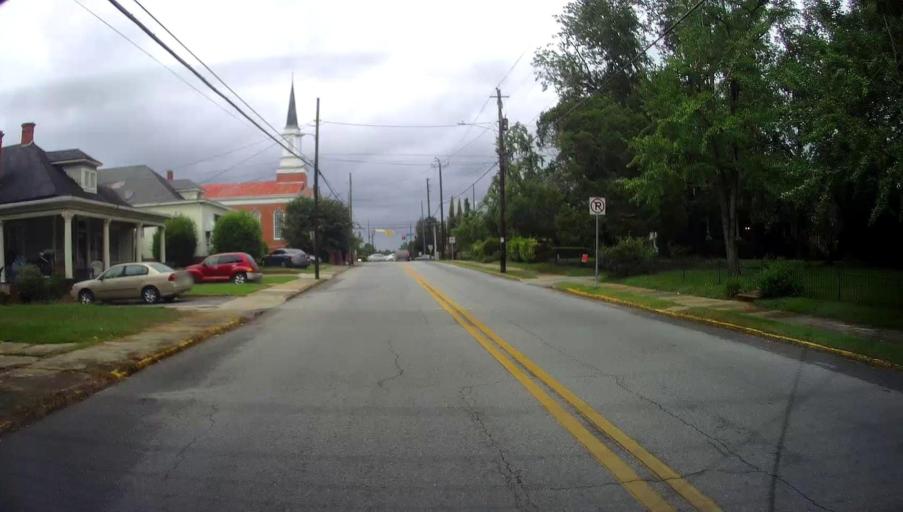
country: US
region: Georgia
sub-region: Bibb County
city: Macon
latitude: 32.8361
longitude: -83.6612
